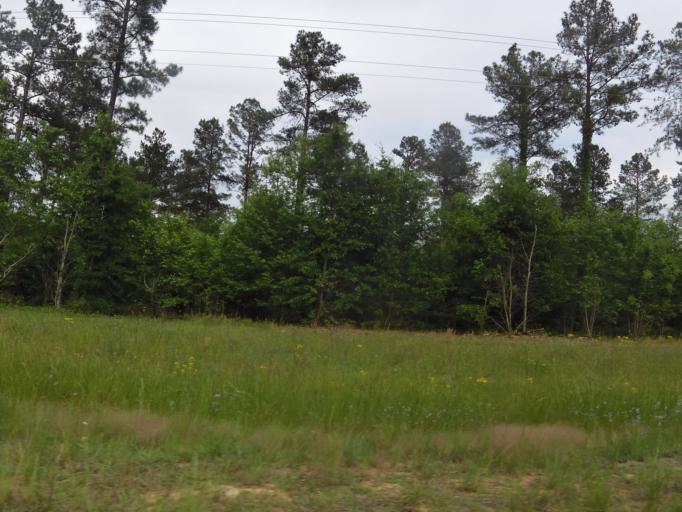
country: US
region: Georgia
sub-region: McDuffie County
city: Thomson
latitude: 33.3503
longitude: -82.4611
